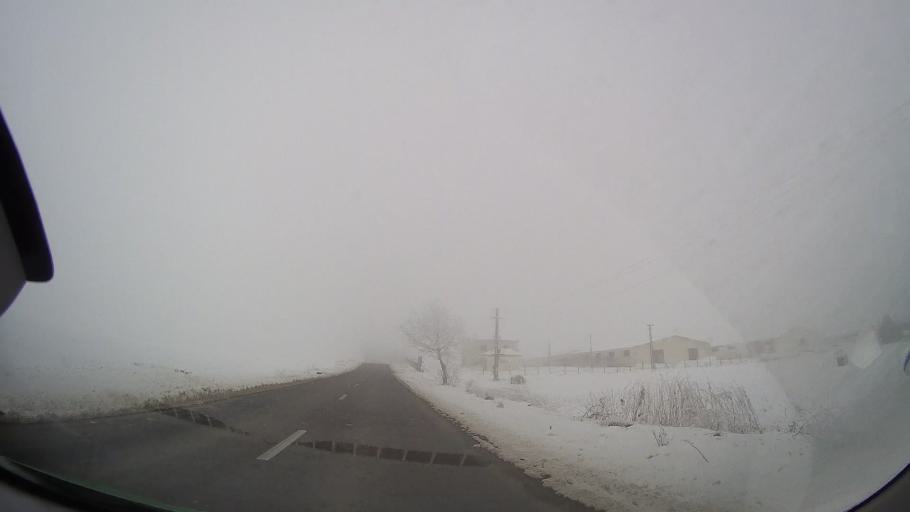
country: RO
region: Iasi
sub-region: Comuna Mogosesti-Siret
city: Mogosesti-Siret
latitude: 47.1456
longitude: 26.7787
